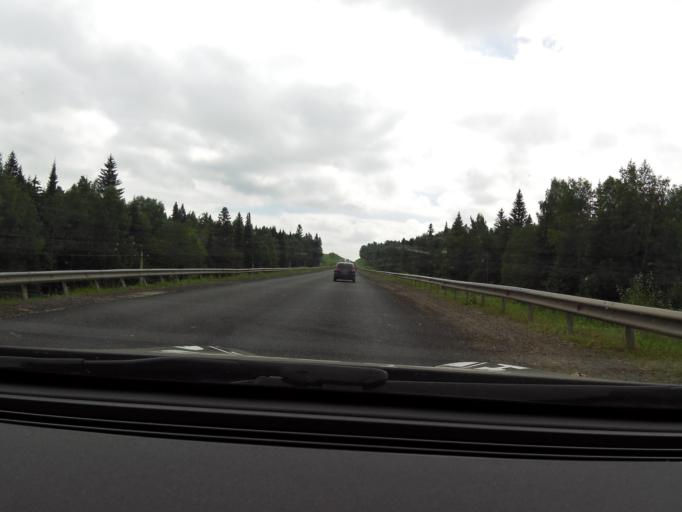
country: RU
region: Perm
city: Bershet'
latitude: 57.7588
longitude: 56.3625
